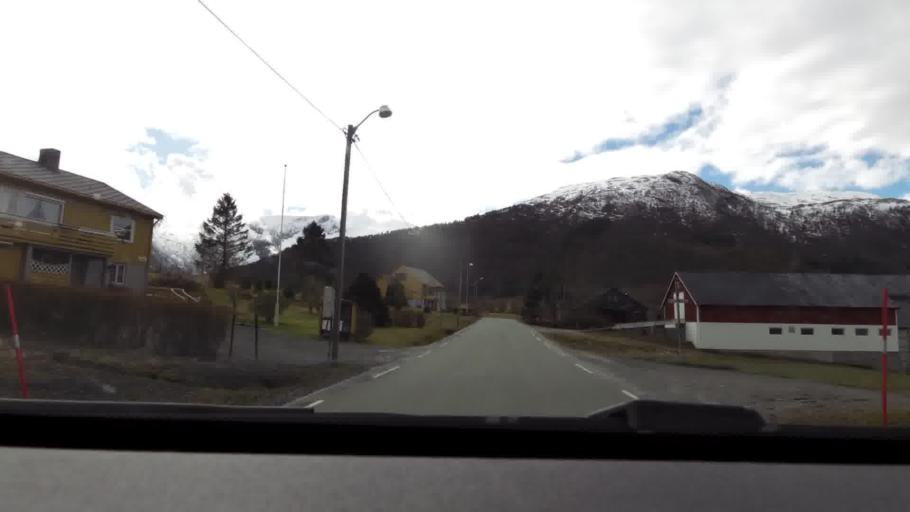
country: NO
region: More og Romsdal
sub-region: Eide
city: Eide
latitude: 62.9116
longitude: 7.5408
